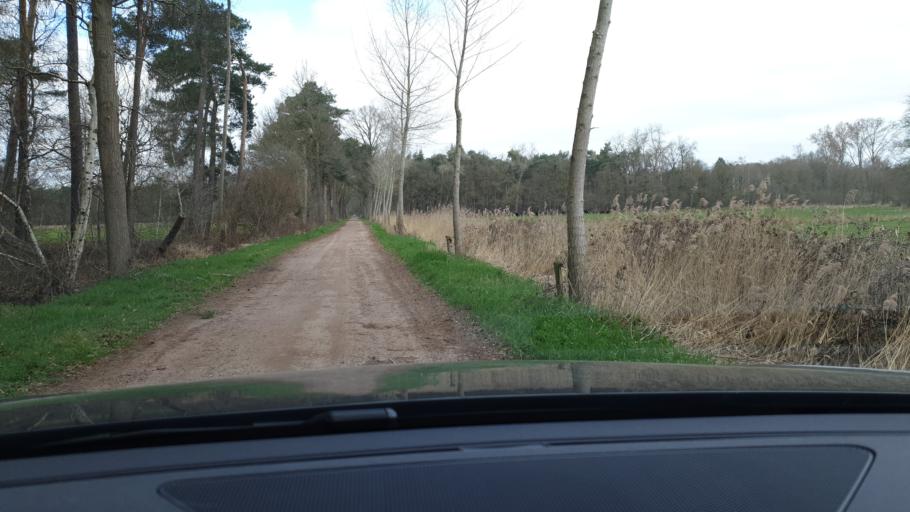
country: NL
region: North Brabant
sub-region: Gemeente Best
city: Best
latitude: 51.5326
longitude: 5.3629
